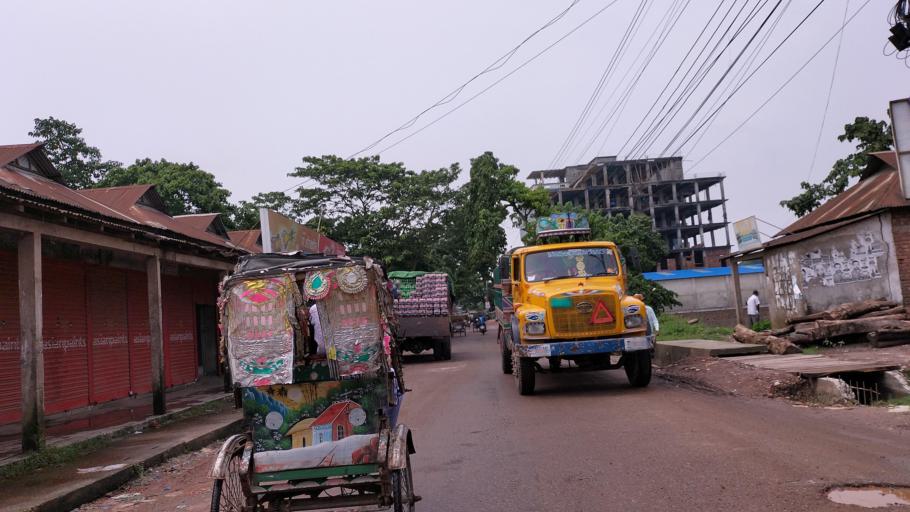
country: BD
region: Dhaka
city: Netrakona
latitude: 24.8912
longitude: 90.7388
